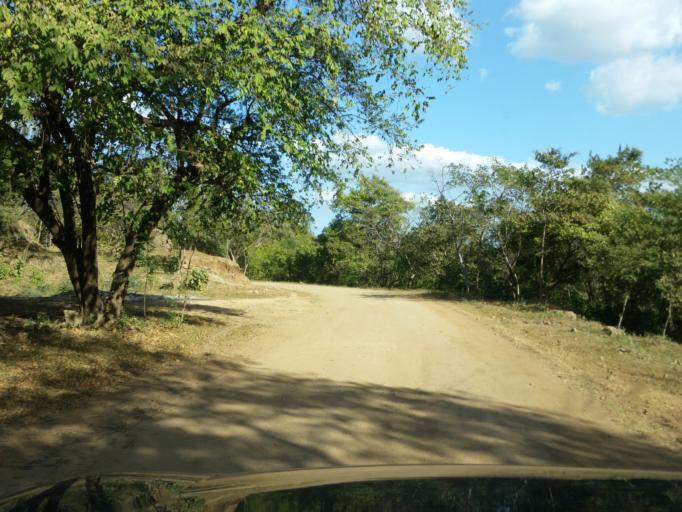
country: NI
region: Managua
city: Carlos Fonseca Amador
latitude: 11.9231
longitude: -86.5904
